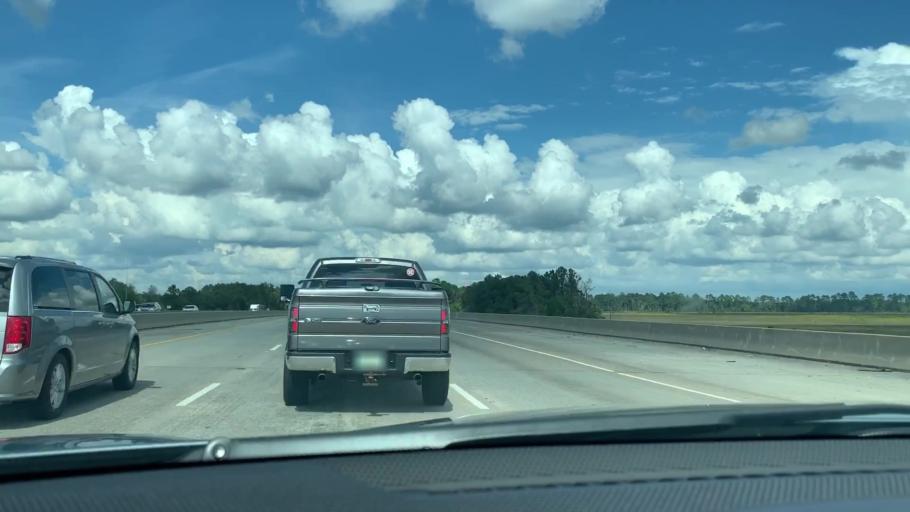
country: US
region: Georgia
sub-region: Camden County
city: Woodbine
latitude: 31.0369
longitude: -81.6531
